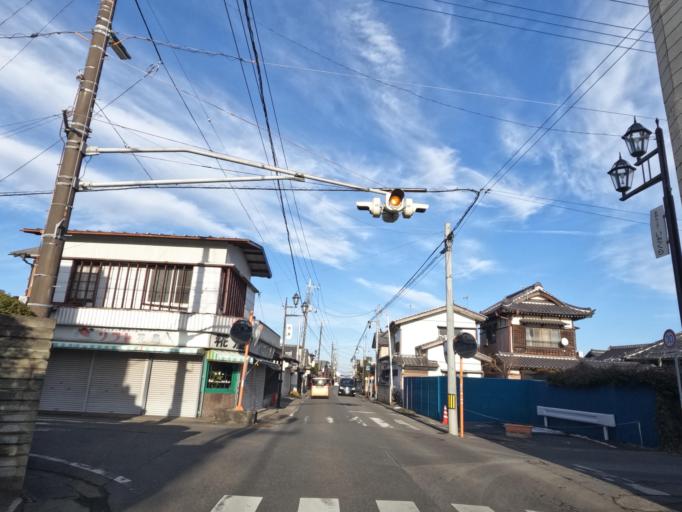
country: JP
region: Ibaraki
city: Toride
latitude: 35.9351
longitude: 140.0663
